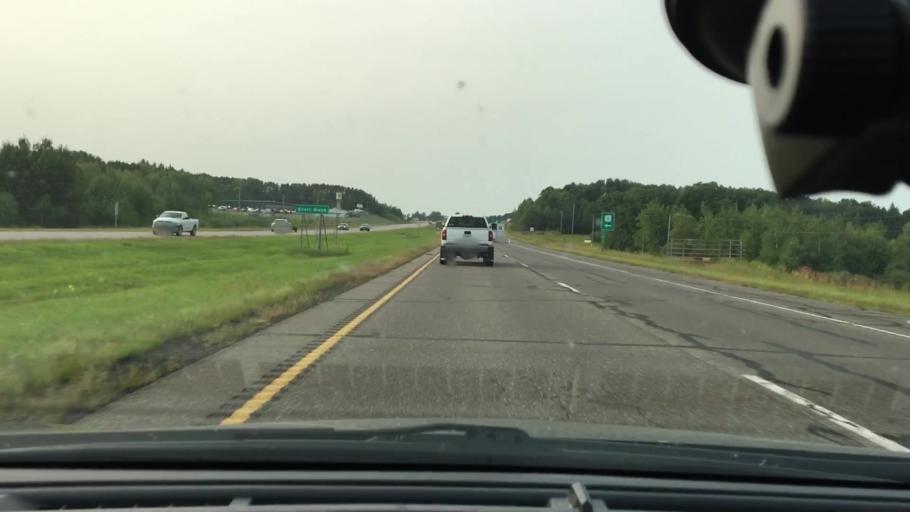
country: US
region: Minnesota
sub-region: Mille Lacs County
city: Milaca
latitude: 45.7760
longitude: -93.6473
